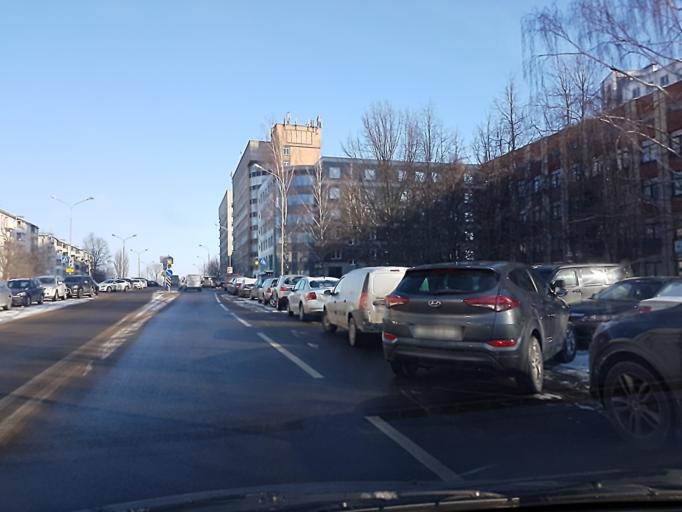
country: BY
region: Minsk
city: Minsk
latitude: 53.9099
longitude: 27.5160
